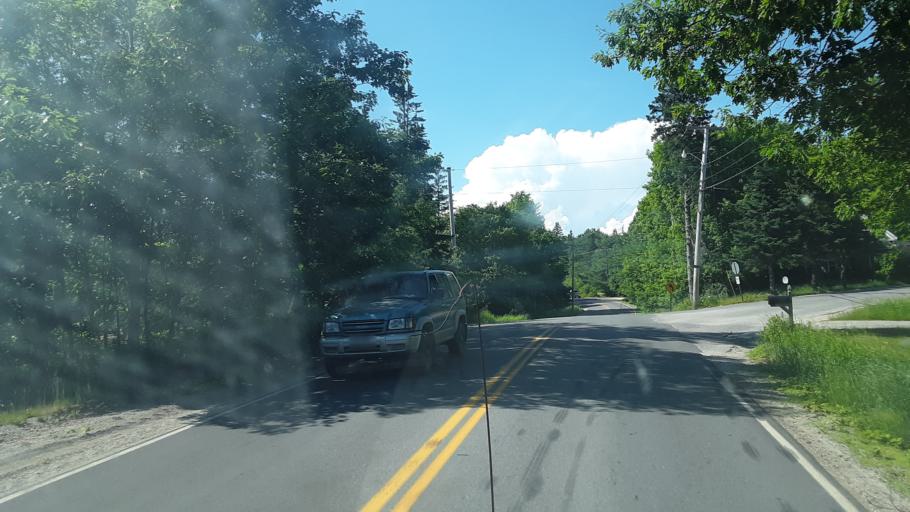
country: US
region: Maine
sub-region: Washington County
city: Cherryfield
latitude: 44.6156
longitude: -67.9252
